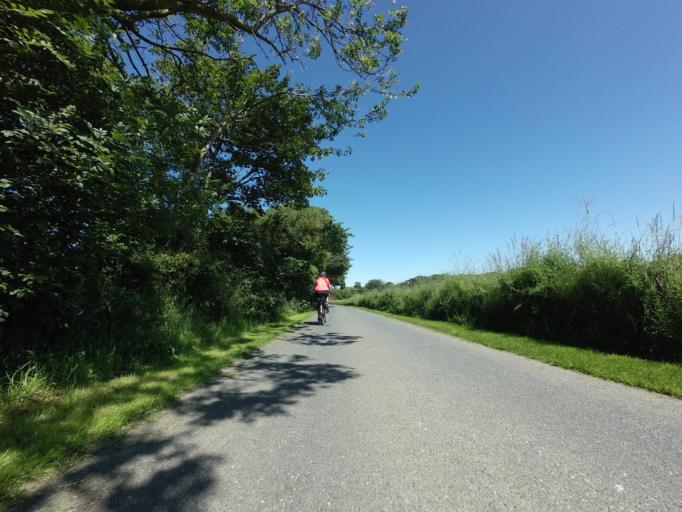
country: GB
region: Scotland
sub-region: Aberdeenshire
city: Macduff
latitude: 57.6595
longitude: -2.4963
